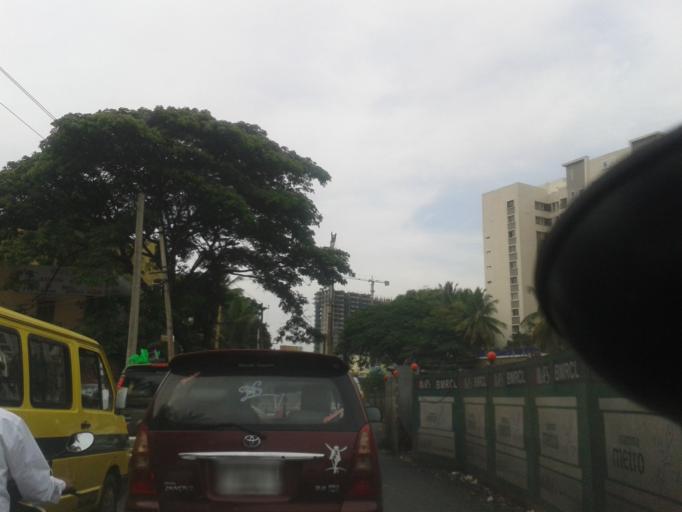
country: IN
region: Karnataka
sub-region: Bangalore Urban
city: Bangalore
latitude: 12.9387
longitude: 77.5225
